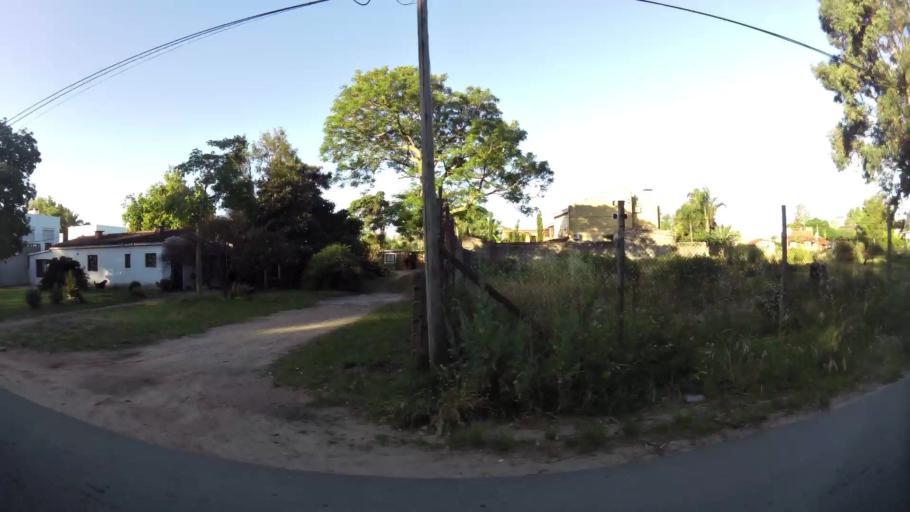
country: UY
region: Canelones
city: Paso de Carrasco
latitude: -34.8509
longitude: -56.0280
